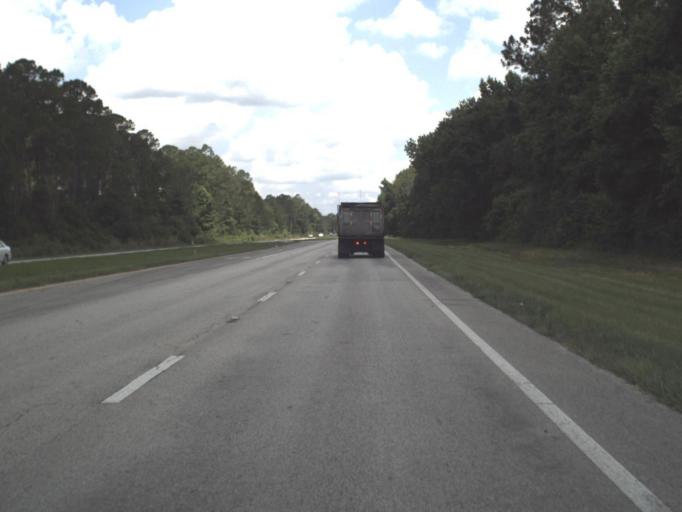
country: US
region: Florida
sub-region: Alachua County
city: Alachua
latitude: 29.7261
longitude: -82.3703
